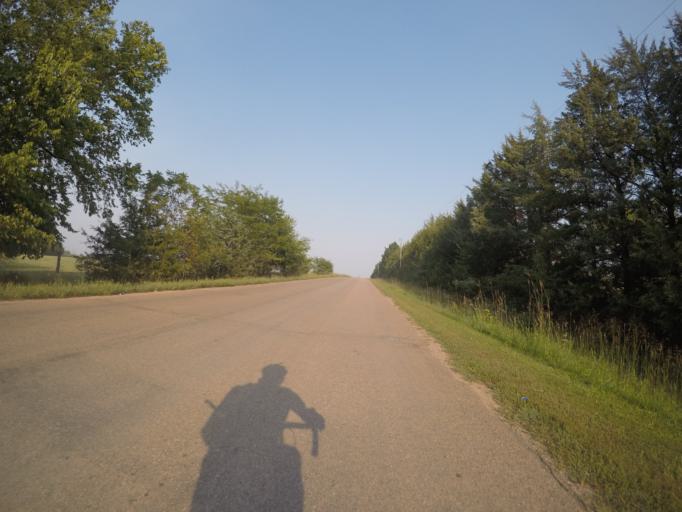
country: US
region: Nebraska
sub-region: Gage County
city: Beatrice
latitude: 40.2628
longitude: -96.7911
